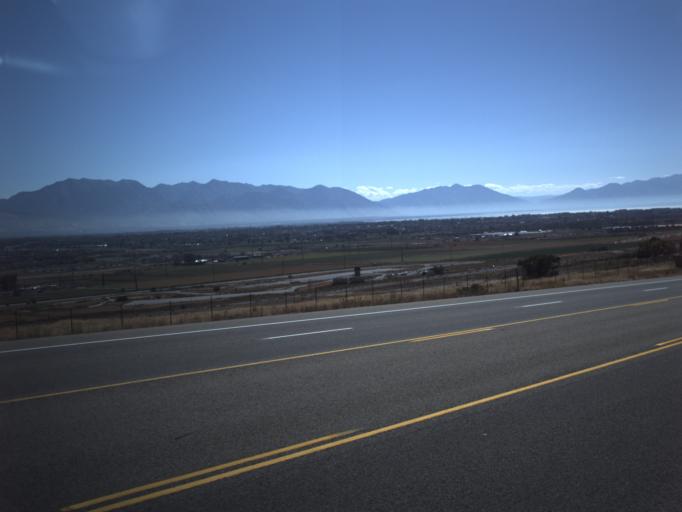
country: US
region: Utah
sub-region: Salt Lake County
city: Bluffdale
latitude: 40.4288
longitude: -111.9277
